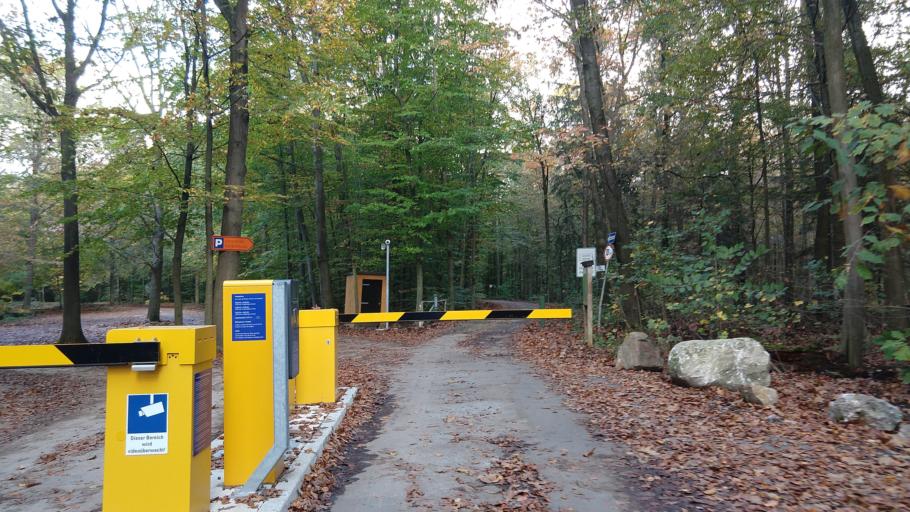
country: DE
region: North Rhine-Westphalia
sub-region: Regierungsbezirk Koln
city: Hurth
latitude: 50.8404
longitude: 6.8677
